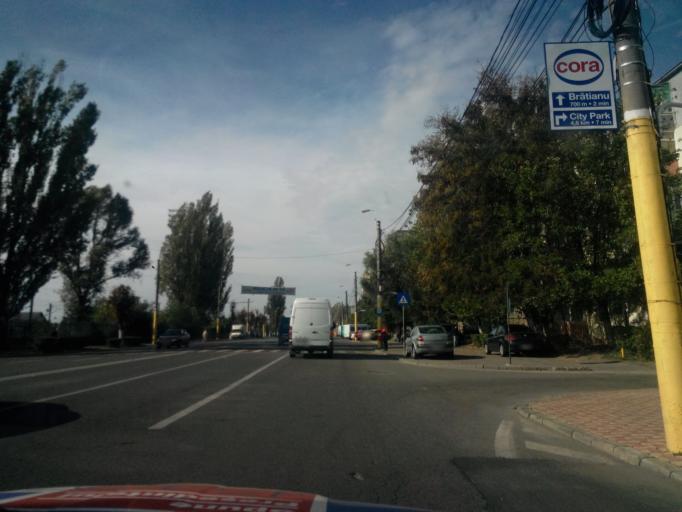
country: RO
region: Constanta
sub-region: Municipiul Constanta
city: Constanta
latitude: 44.1717
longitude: 28.6215
